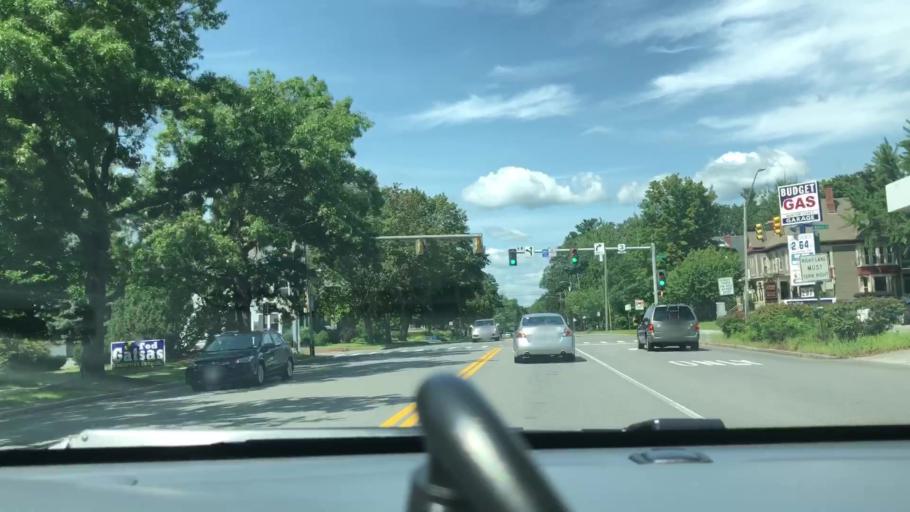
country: US
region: New Hampshire
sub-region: Hillsborough County
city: Manchester
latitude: 43.0059
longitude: -71.4653
